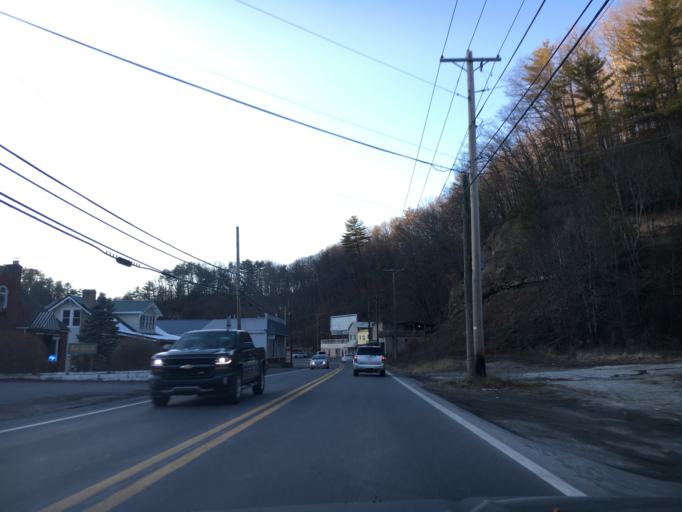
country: US
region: West Virginia
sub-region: Raleigh County
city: Beaver
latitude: 37.7508
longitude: -81.1427
